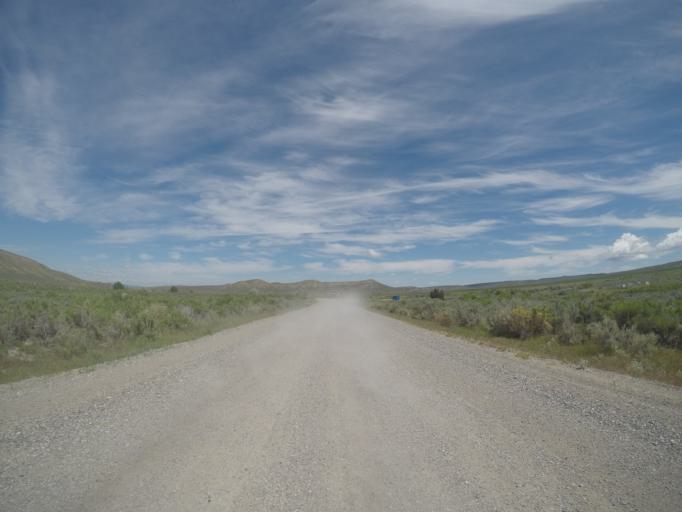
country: US
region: Montana
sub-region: Carbon County
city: Red Lodge
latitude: 45.2227
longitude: -108.8419
